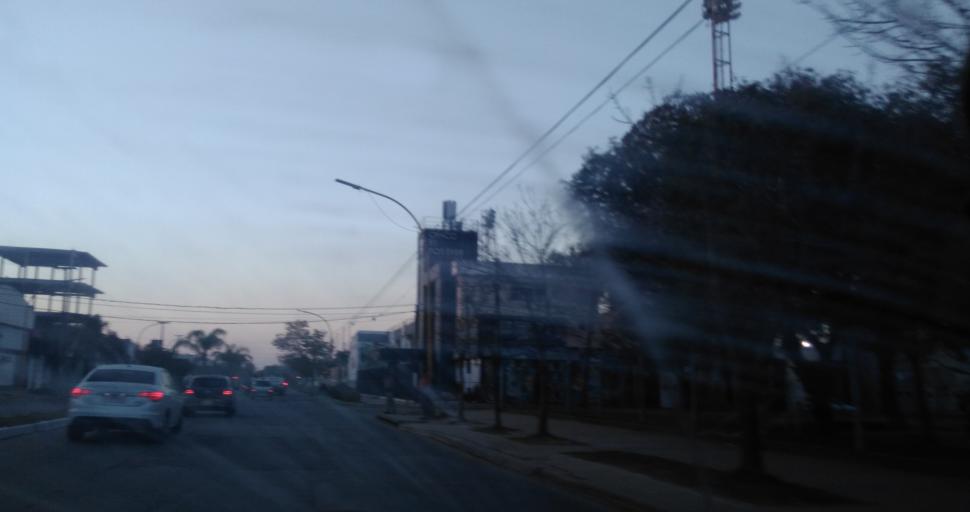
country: AR
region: Chaco
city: Resistencia
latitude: -27.4685
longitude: -58.9671
